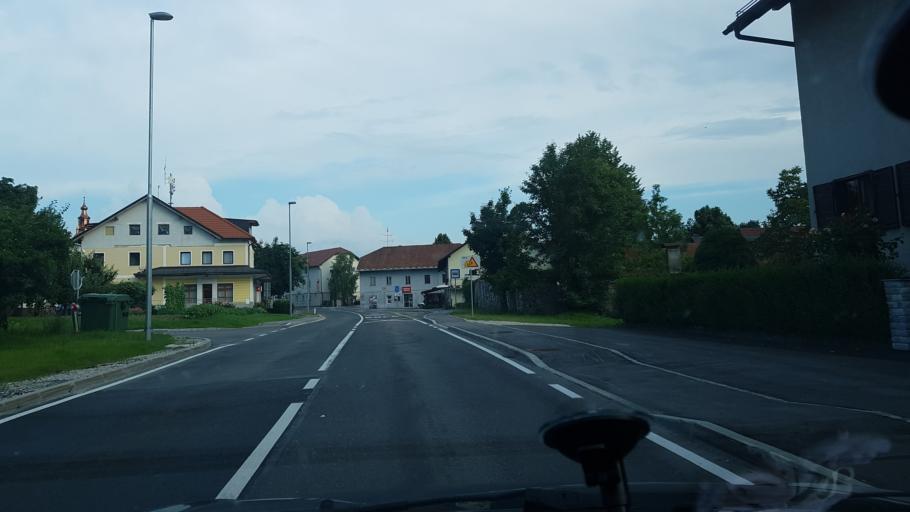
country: SI
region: Idrija
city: Idrija
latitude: 45.9585
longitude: 14.0917
